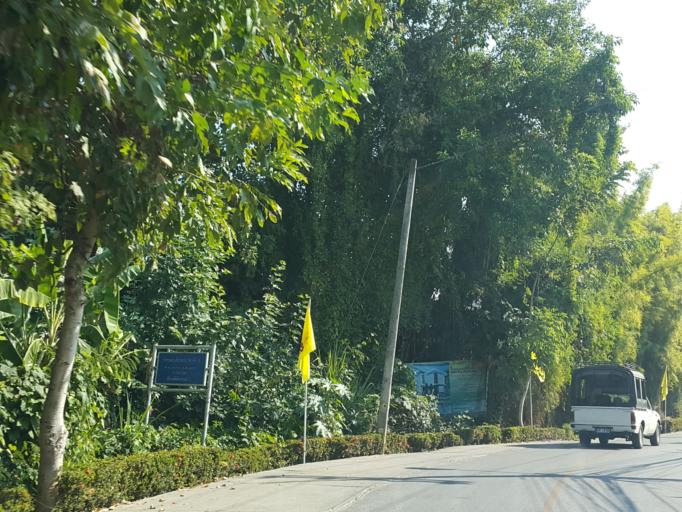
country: TH
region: Chiang Mai
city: San Sai
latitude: 18.8488
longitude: 99.0238
